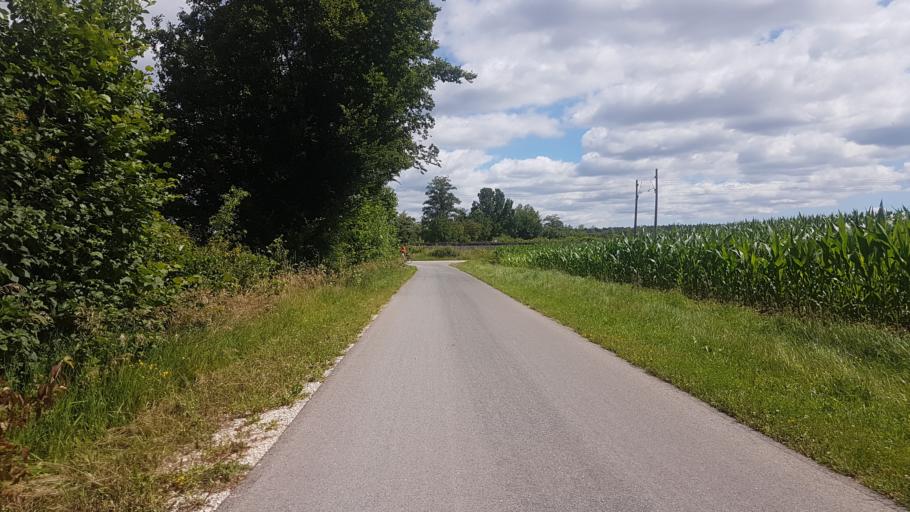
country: DE
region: Bavaria
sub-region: Regierungsbezirk Mittelfranken
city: Gunzenhausen
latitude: 49.1294
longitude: 10.7640
